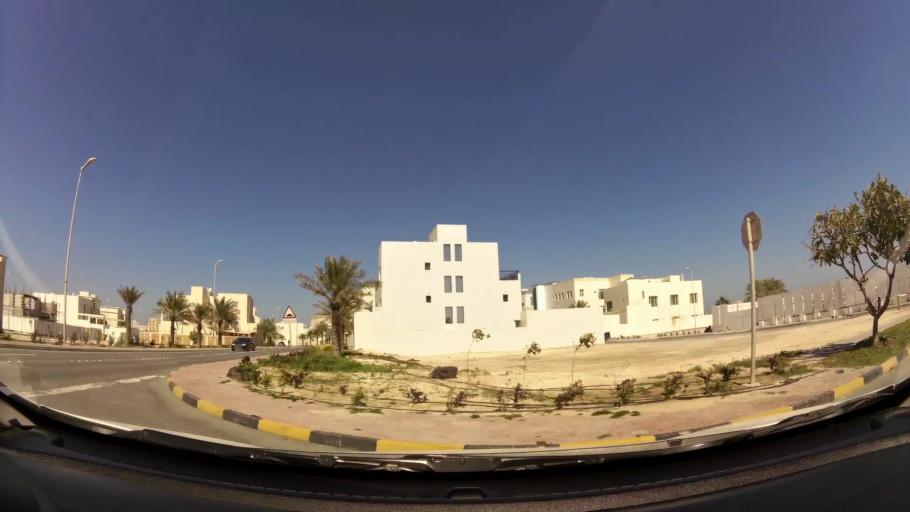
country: BH
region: Muharraq
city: Al Hadd
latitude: 26.2886
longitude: 50.6739
